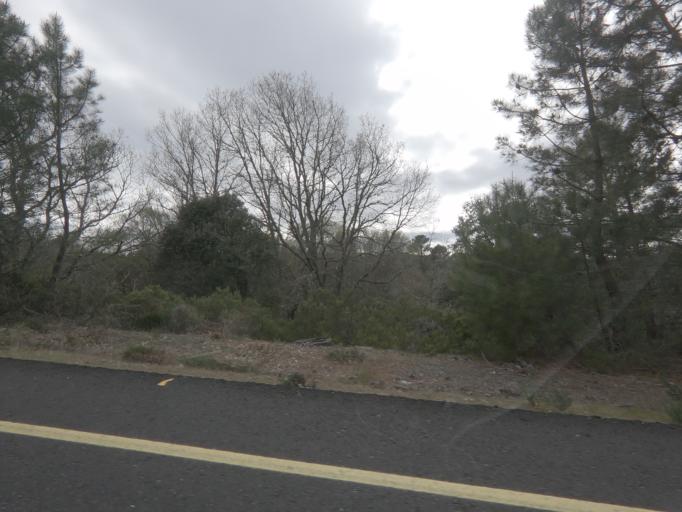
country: ES
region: Extremadura
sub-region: Provincia de Caceres
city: Acebo
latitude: 40.2506
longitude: -6.6888
